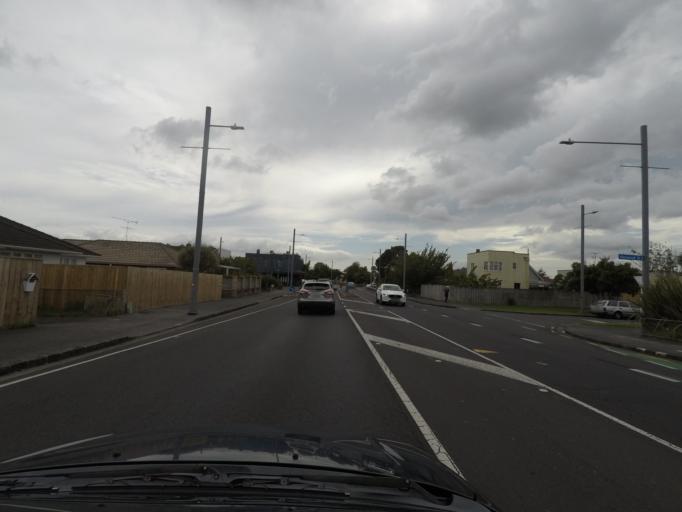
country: NZ
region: Auckland
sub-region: Auckland
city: Auckland
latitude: -36.8938
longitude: 174.7359
